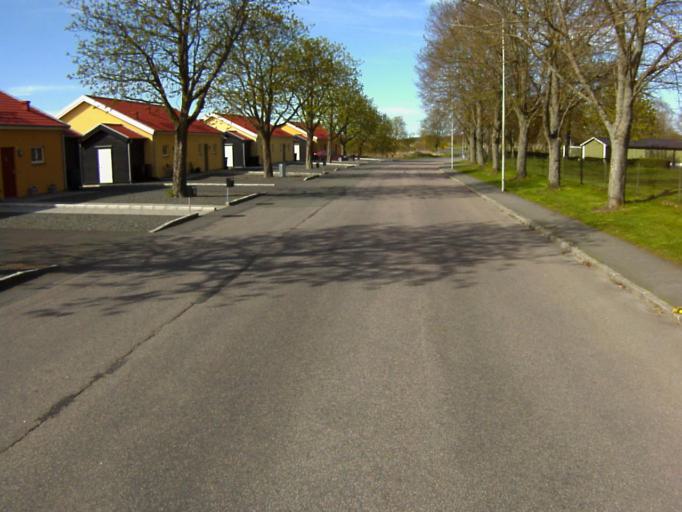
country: SE
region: Skane
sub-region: Kristianstads Kommun
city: Kristianstad
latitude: 56.0593
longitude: 14.1515
